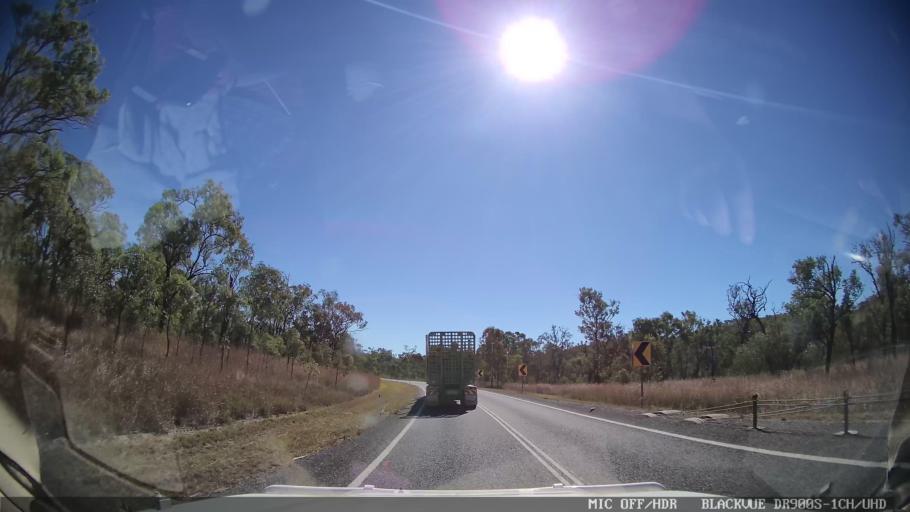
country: AU
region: Queensland
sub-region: Gladstone
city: Toolooa
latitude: -24.1512
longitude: 151.2099
